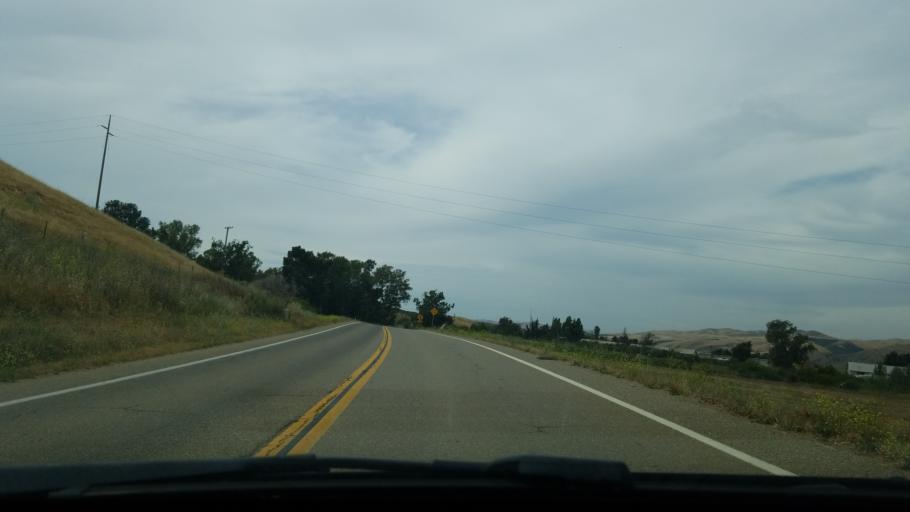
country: US
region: California
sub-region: Santa Barbara County
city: Orcutt
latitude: 34.8811
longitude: -120.3135
